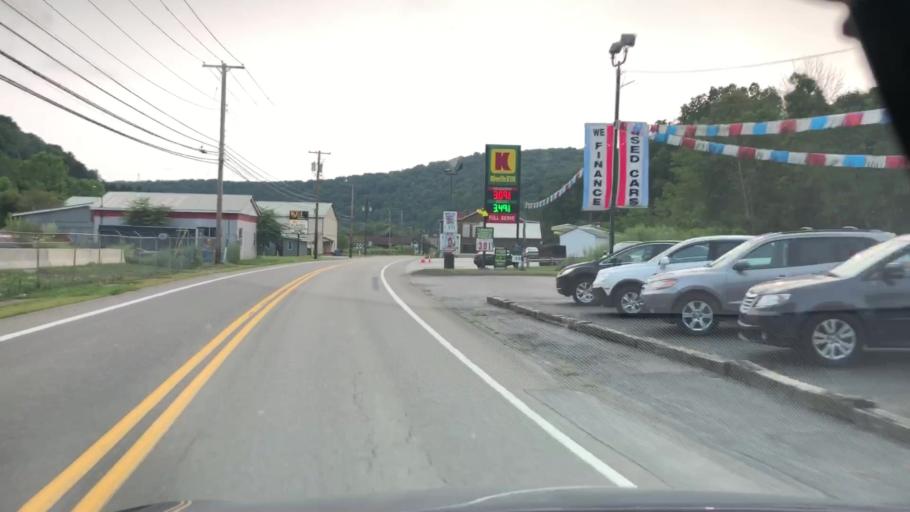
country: US
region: Pennsylvania
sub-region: Venango County
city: Oil City
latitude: 41.4457
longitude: -79.6946
